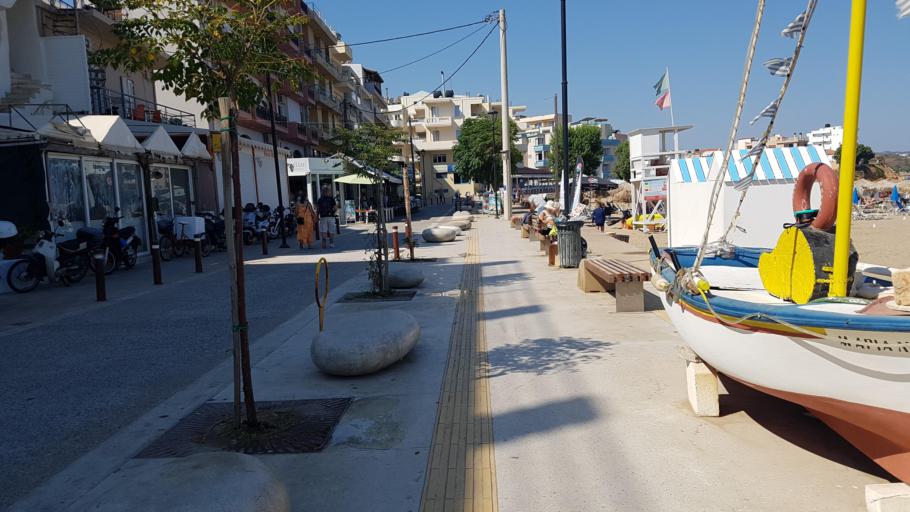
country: GR
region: Crete
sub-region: Nomos Chanias
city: Chania
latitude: 35.5139
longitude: 24.0068
